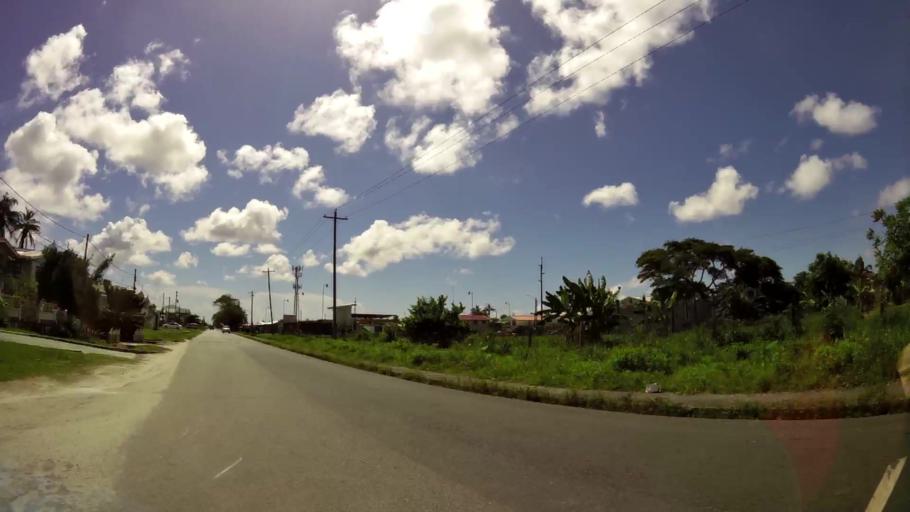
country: GY
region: Demerara-Mahaica
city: Georgetown
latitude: 6.7857
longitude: -58.1381
